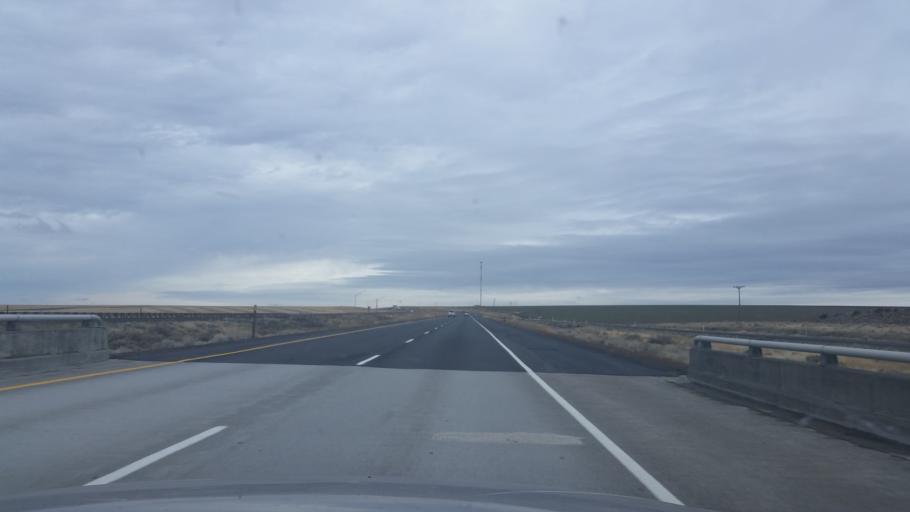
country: US
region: Washington
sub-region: Adams County
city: Ritzville
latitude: 47.0973
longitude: -118.6675
